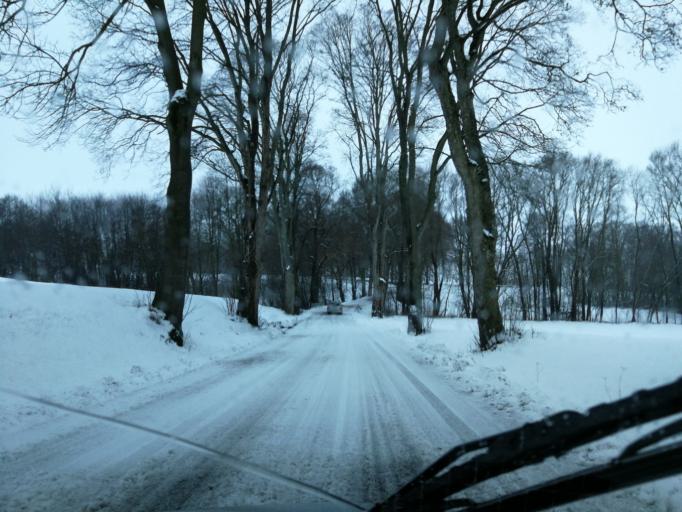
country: CZ
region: Vysocina
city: Heralec
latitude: 49.5337
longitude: 15.4433
